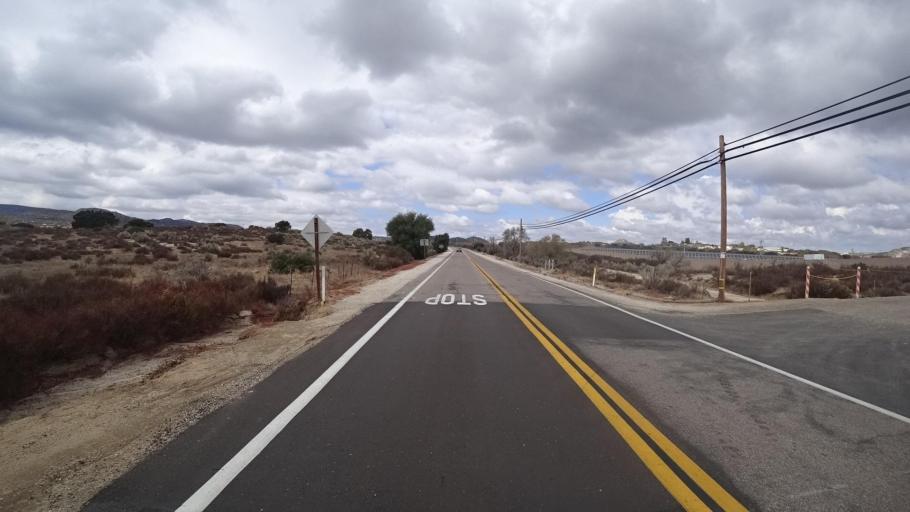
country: US
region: California
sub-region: San Diego County
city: Campo
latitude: 32.6306
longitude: -116.4733
